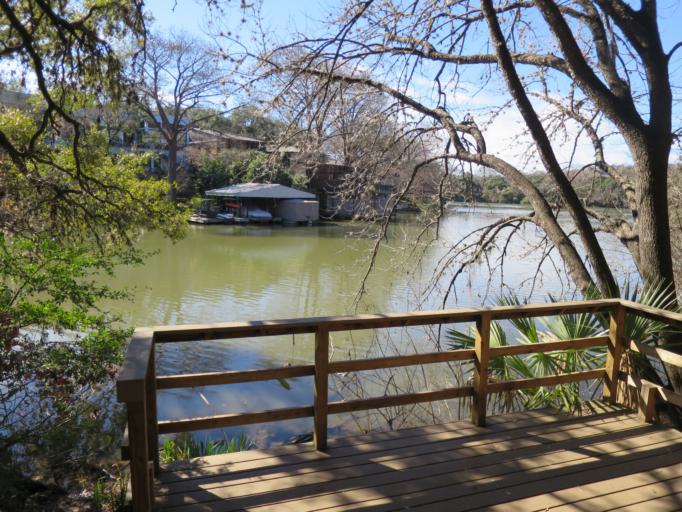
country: US
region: Texas
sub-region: Travis County
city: West Lake Hills
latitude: 30.3118
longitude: -97.7718
